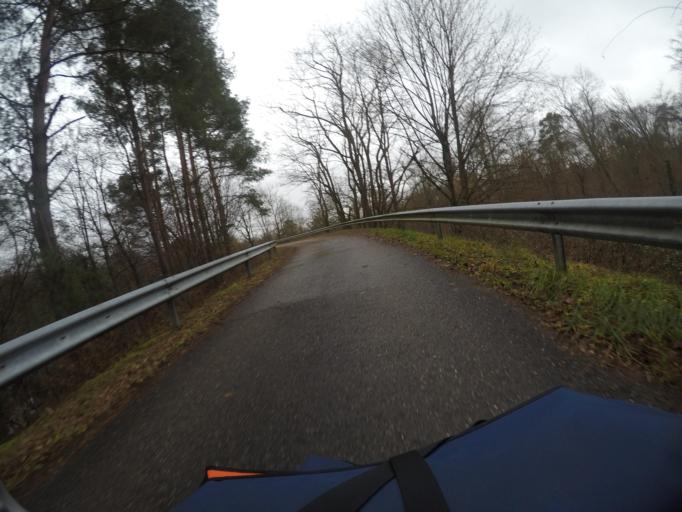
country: DE
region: Baden-Wuerttemberg
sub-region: Karlsruhe Region
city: Graben-Neudorf
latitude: 49.2058
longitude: 8.4977
